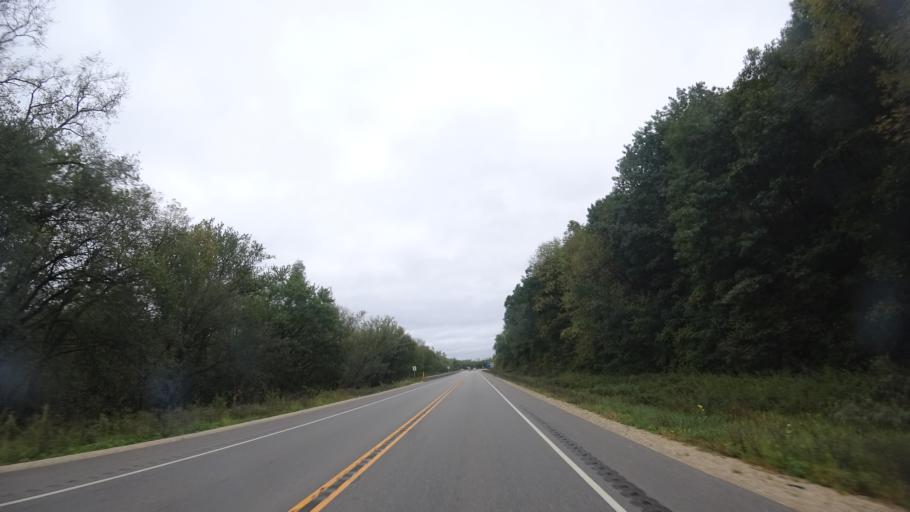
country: US
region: Wisconsin
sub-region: Grant County
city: Boscobel
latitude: 43.1560
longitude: -90.7126
